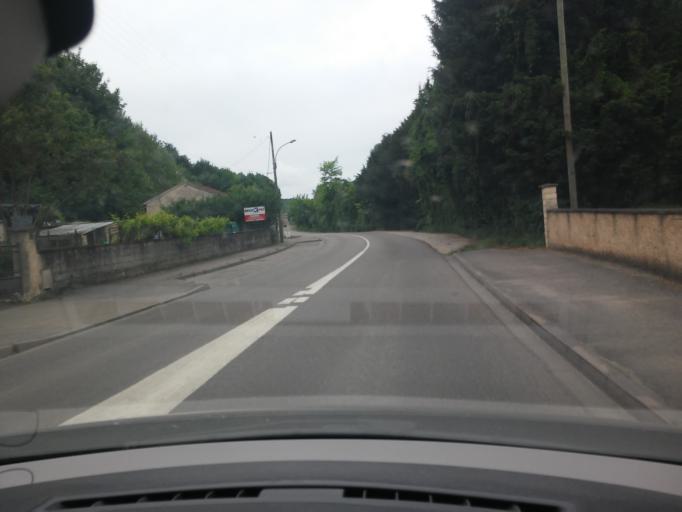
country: FR
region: Lorraine
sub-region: Departement de la Meuse
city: Commercy
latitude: 48.7683
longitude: 5.5796
